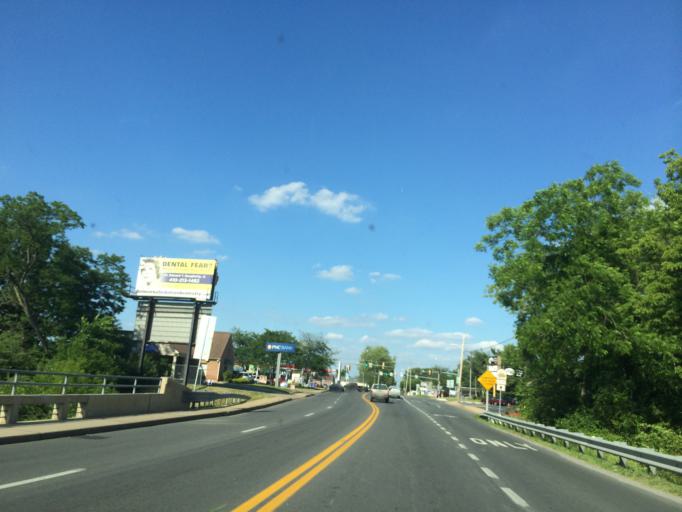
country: US
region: Maryland
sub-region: Wicomico County
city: Salisbury
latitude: 38.3691
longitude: -75.6161
